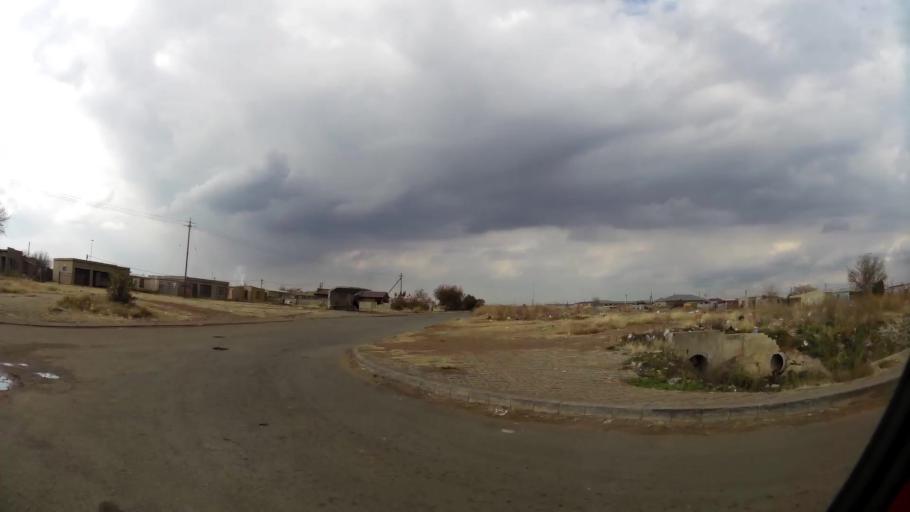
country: ZA
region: Gauteng
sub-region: Sedibeng District Municipality
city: Vanderbijlpark
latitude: -26.6823
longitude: 27.7817
